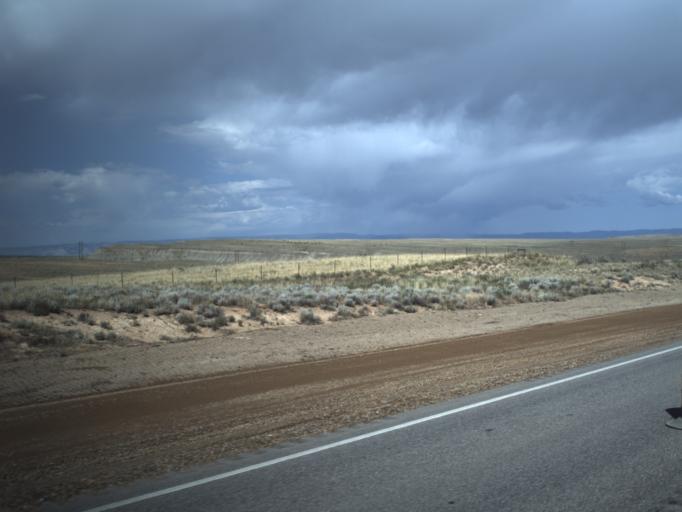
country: US
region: Utah
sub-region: Carbon County
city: East Carbon City
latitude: 39.4470
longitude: -110.4711
